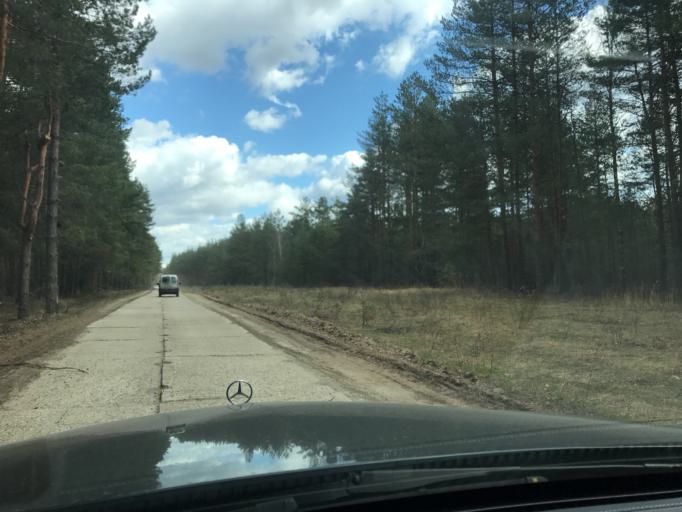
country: RU
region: Vladimir
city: Pokrov
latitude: 55.8676
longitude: 39.2301
